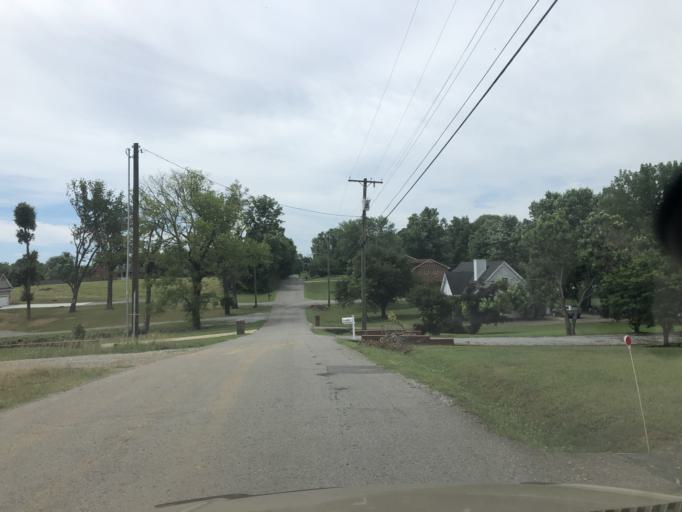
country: US
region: Tennessee
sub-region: Davidson County
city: Lakewood
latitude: 36.2556
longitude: -86.6153
